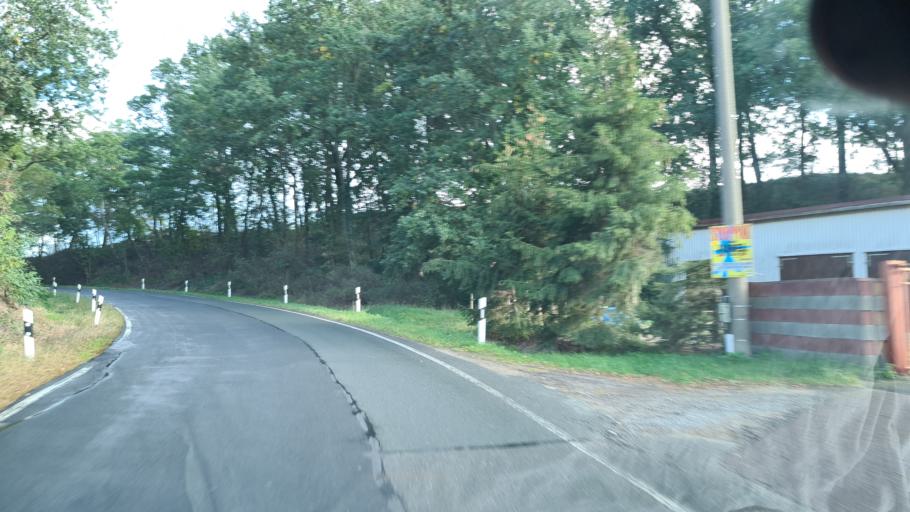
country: DE
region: Saxony
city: Dahlen
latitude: 51.3639
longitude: 13.0094
